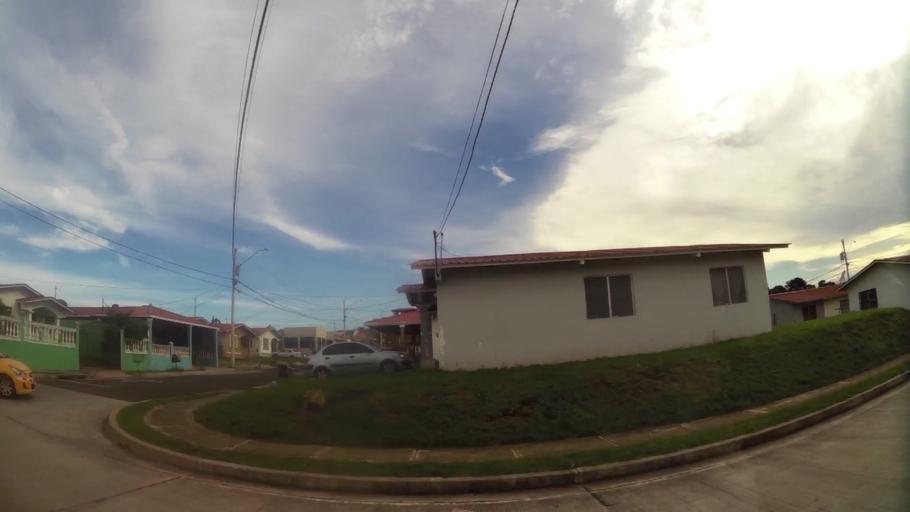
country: PA
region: Panama
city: La Chorrera
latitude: 8.8822
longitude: -79.7676
